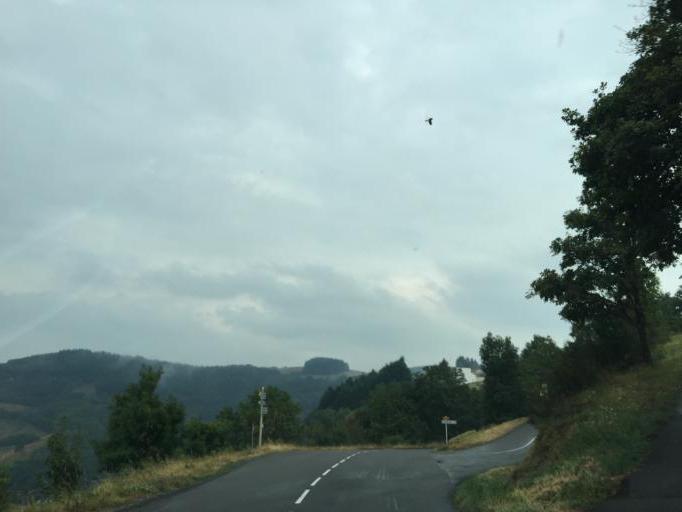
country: FR
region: Rhone-Alpes
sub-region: Departement de la Loire
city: Saint-Christo-en-Jarez
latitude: 45.5296
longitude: 4.4919
